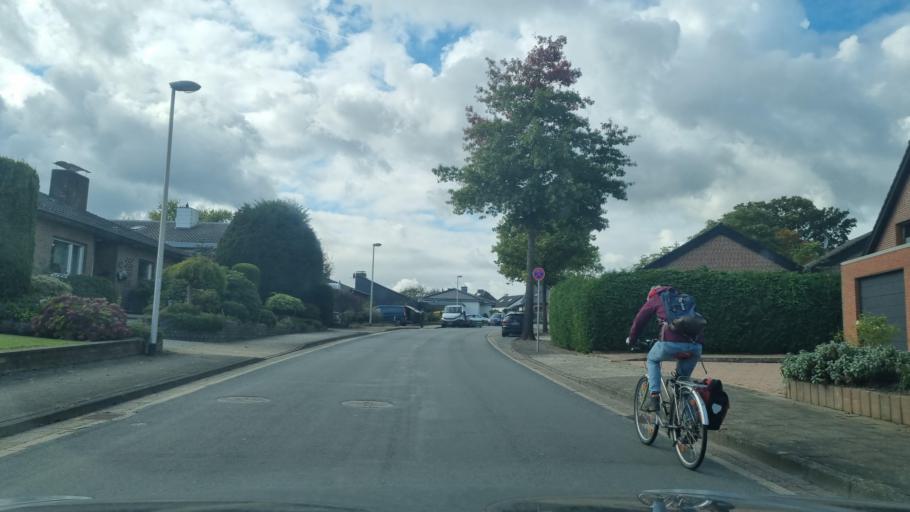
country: DE
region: North Rhine-Westphalia
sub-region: Regierungsbezirk Dusseldorf
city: Kleve
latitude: 51.7778
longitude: 6.1096
